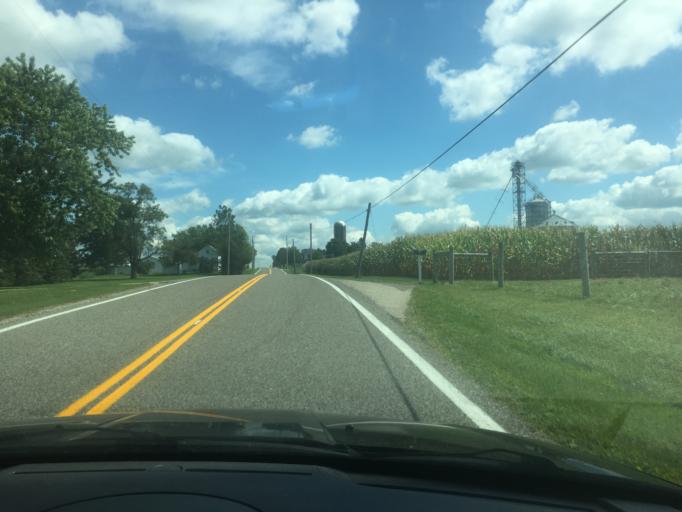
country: US
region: Ohio
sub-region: Logan County
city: West Liberty
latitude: 40.2318
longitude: -83.7160
